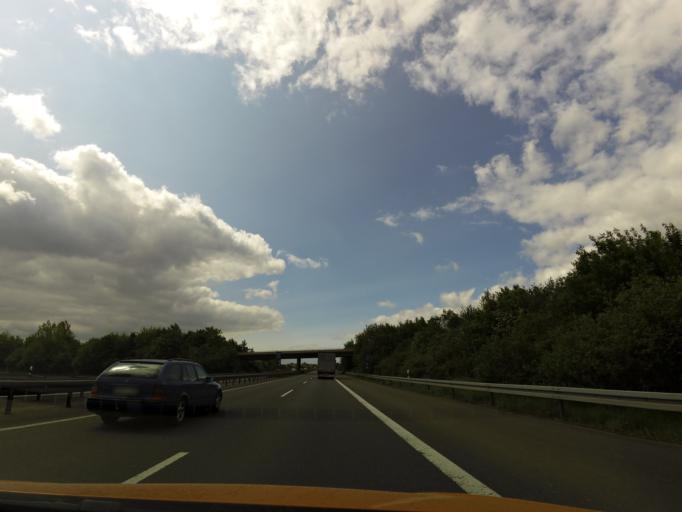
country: DE
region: Lower Saxony
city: Leiferde
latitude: 52.2024
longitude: 10.4760
